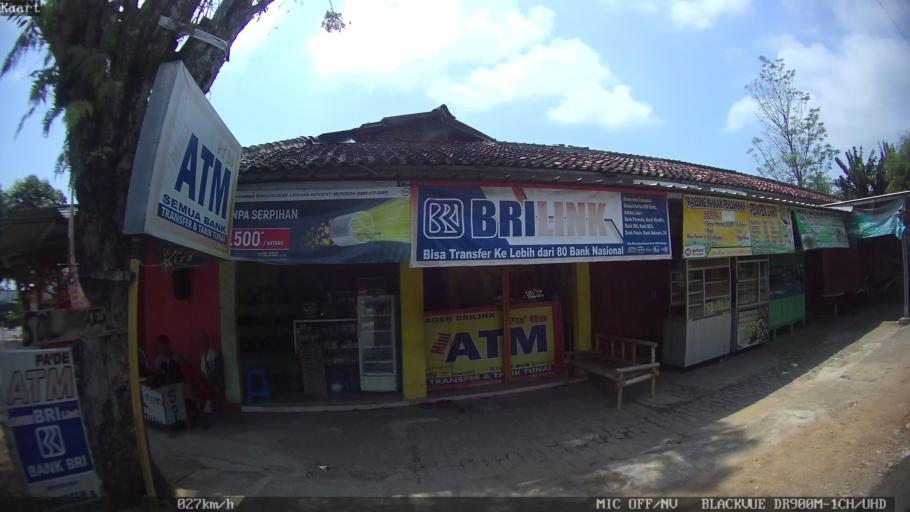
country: ID
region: Lampung
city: Kedaton
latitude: -5.3775
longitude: 105.2631
